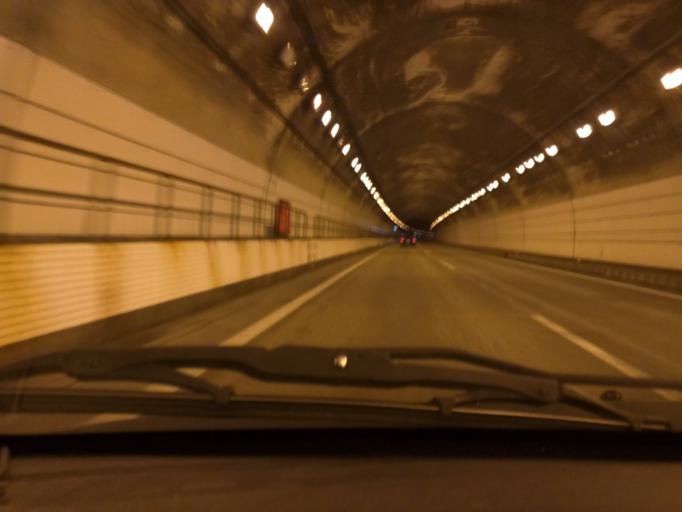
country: JP
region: Nagano
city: Nakano
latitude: 36.7990
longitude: 138.2834
